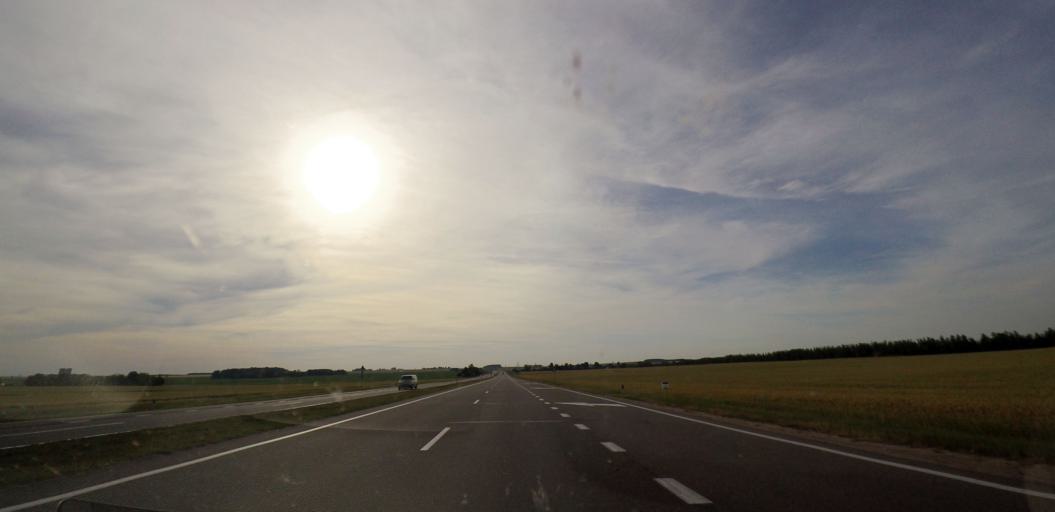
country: BY
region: Grodnenskaya
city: Skidal'
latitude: 53.6130
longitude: 24.0837
